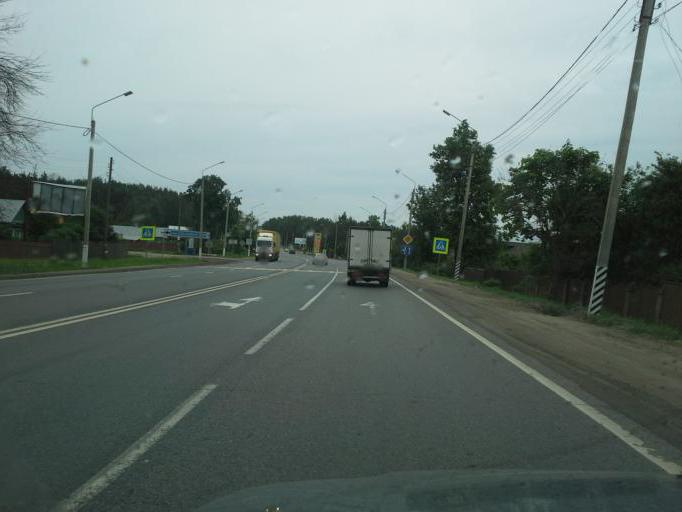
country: RU
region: Vladimir
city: Pokrov
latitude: 55.9004
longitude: 39.0721
